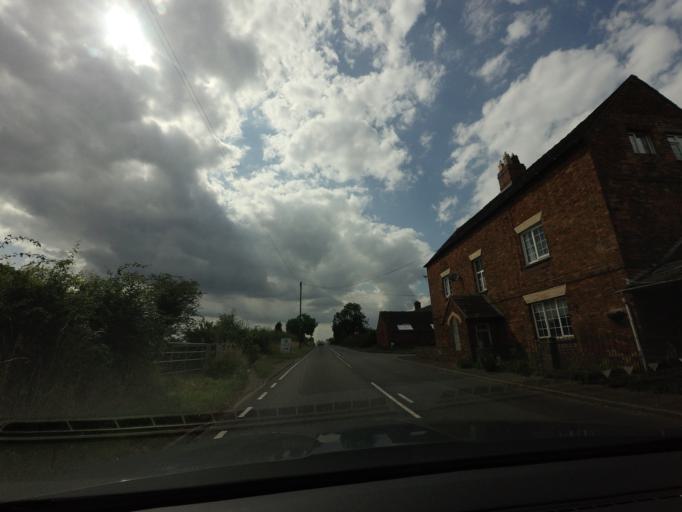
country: GB
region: England
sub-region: Staffordshire
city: Brewood
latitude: 52.6944
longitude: -2.1677
